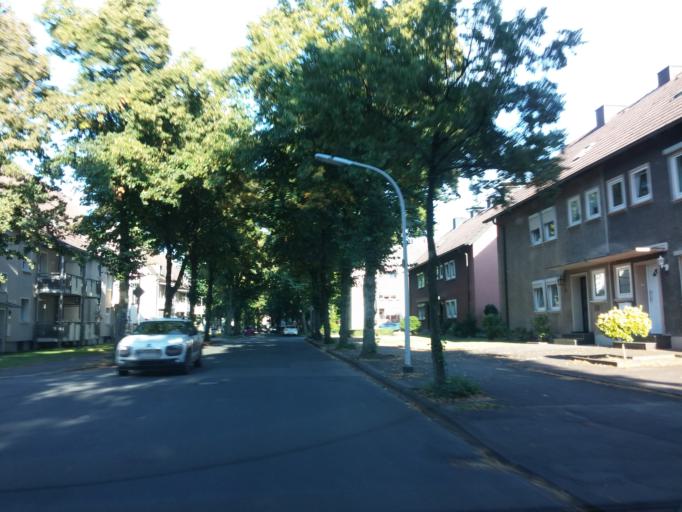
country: DE
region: North Rhine-Westphalia
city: Dorsten
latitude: 51.6781
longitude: 6.9529
